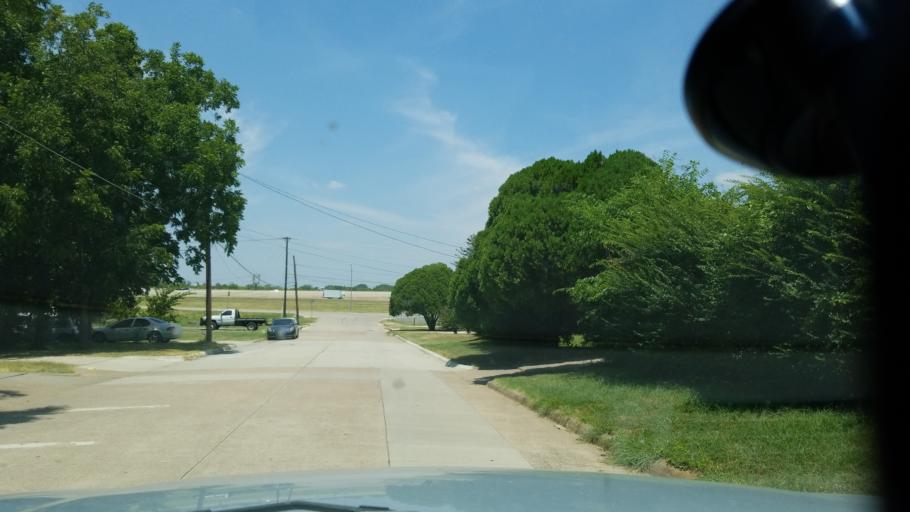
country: US
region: Texas
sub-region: Dallas County
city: Grand Prairie
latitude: 32.7592
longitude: -96.9630
